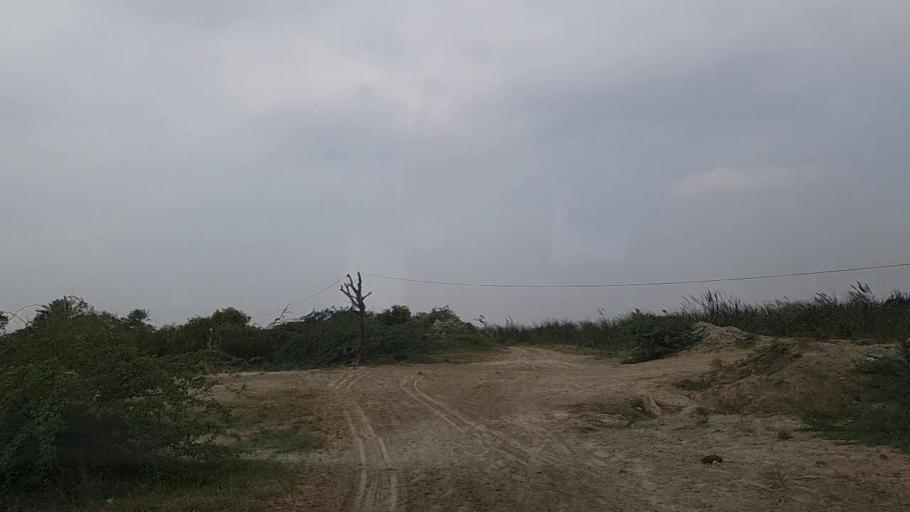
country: PK
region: Sindh
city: Mirpur Sakro
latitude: 24.5959
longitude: 67.6969
